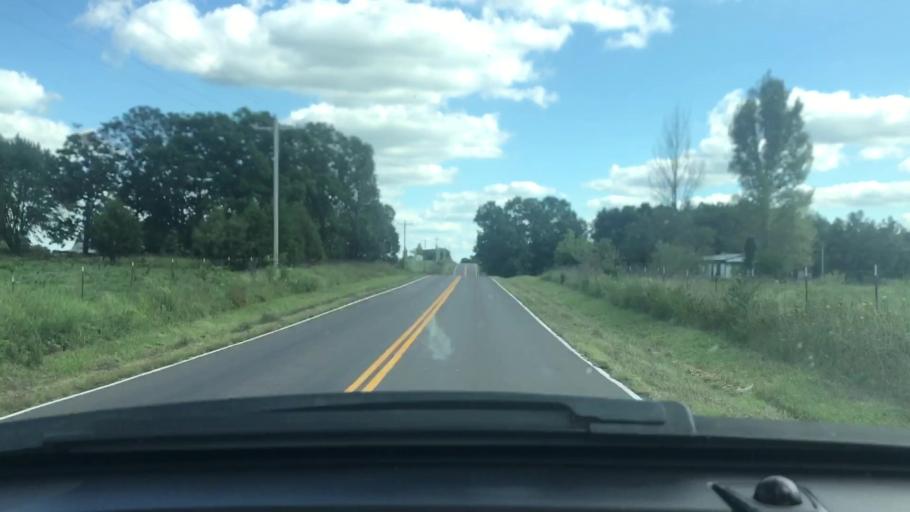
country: US
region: Missouri
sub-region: Wright County
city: Mountain Grove
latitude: 37.3114
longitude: -92.3174
